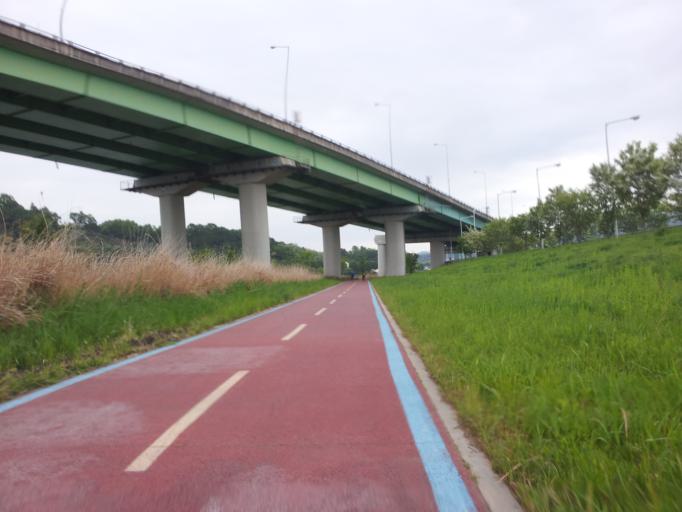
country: KR
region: Daejeon
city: Daejeon
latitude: 36.3721
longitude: 127.3982
